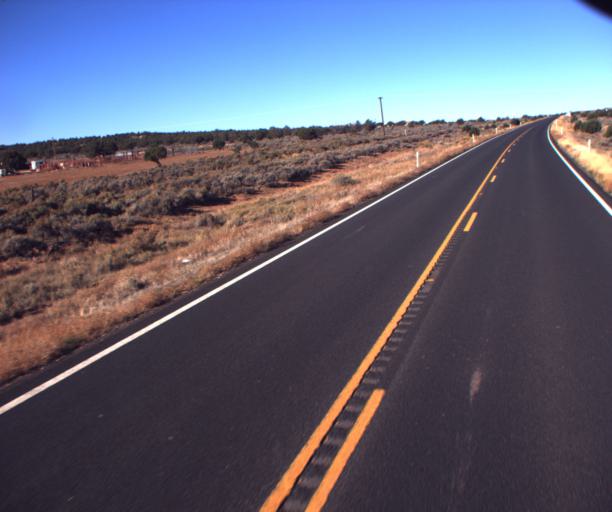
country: US
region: Arizona
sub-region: Apache County
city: Ganado
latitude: 35.7606
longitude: -109.7744
